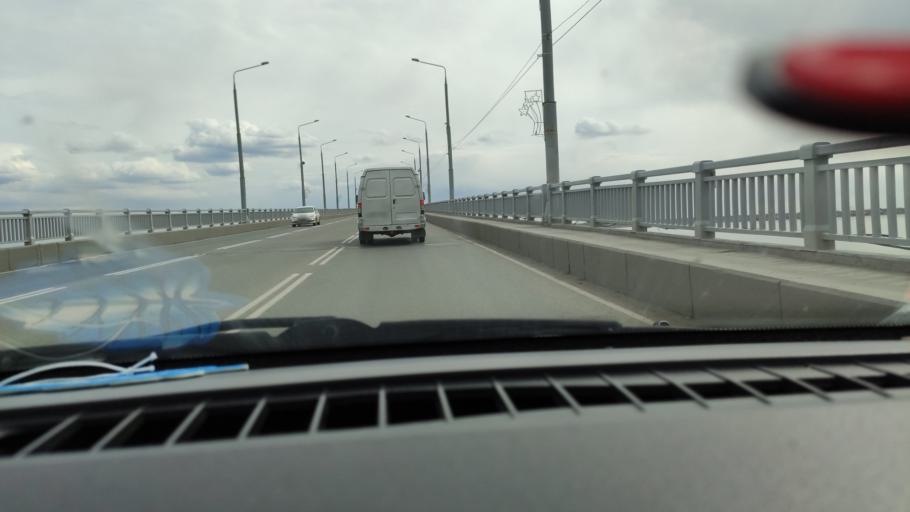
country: RU
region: Saratov
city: Engel's
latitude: 51.5250
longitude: 46.0663
